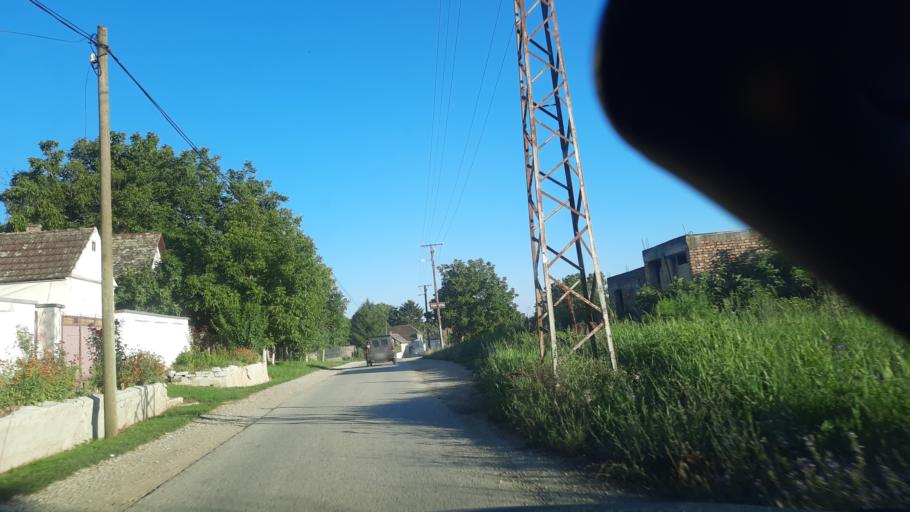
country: RS
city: Cortanovci
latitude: 45.1184
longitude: 19.9449
